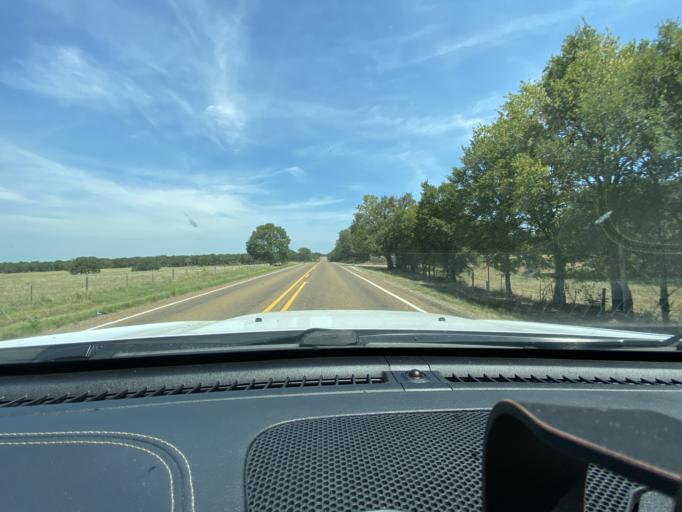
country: US
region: Texas
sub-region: Bastrop County
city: Smithville
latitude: 30.1183
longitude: -97.0814
